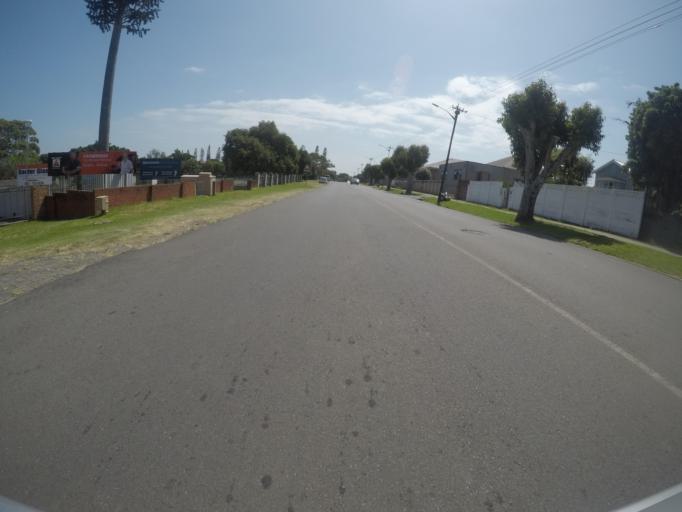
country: ZA
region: Eastern Cape
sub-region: Buffalo City Metropolitan Municipality
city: East London
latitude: -32.9809
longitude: 27.8851
